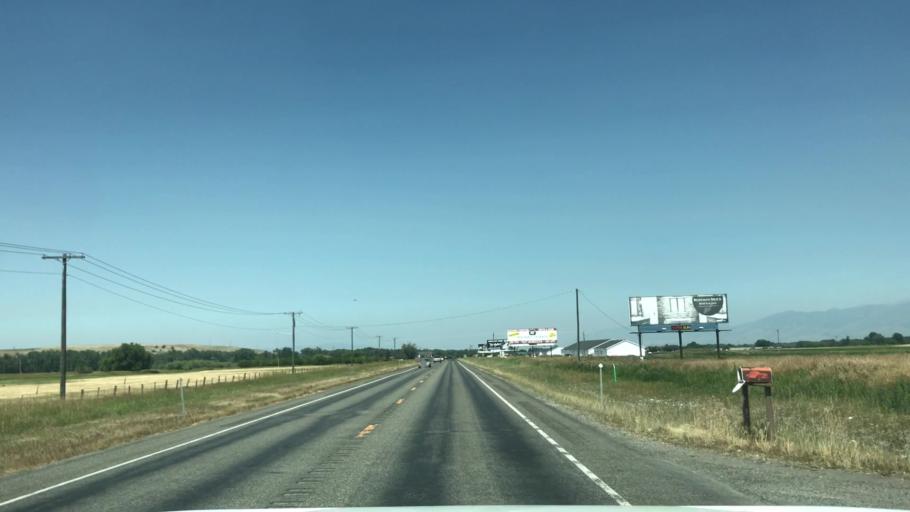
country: US
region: Montana
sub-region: Gallatin County
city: Four Corners
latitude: 45.6314
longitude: -111.1968
